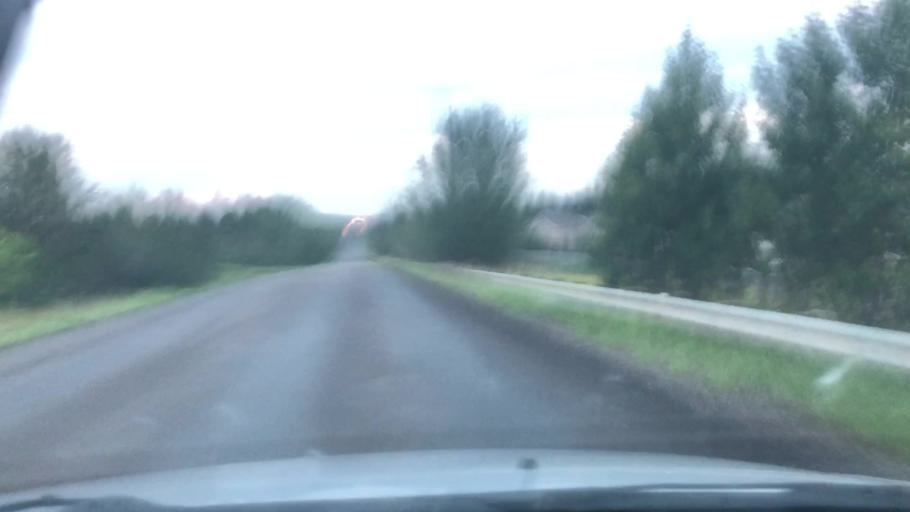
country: CA
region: Alberta
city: Devon
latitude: 53.4856
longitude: -113.6889
